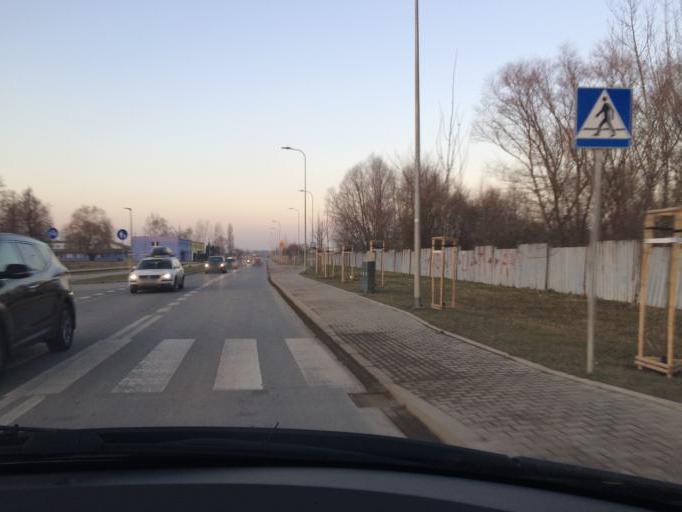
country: PL
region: Lesser Poland Voivodeship
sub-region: Powiat wielicki
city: Czarnochowice
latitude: 50.0283
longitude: 20.0516
